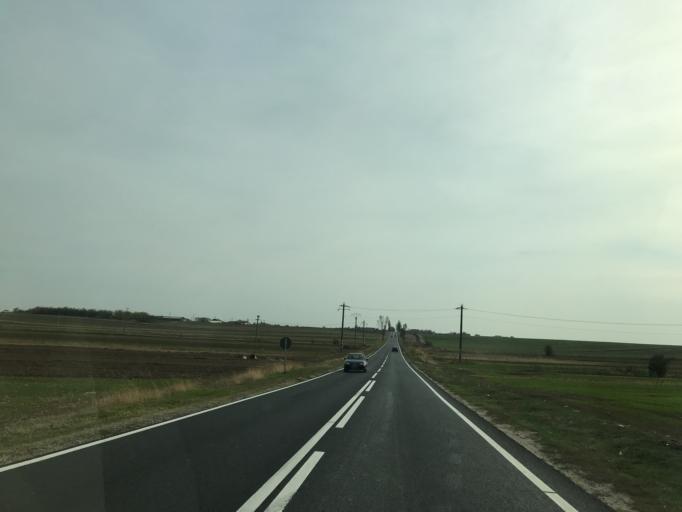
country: RO
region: Olt
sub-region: Comuna Brancoveni
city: Brancoveni
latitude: 44.3251
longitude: 24.2976
